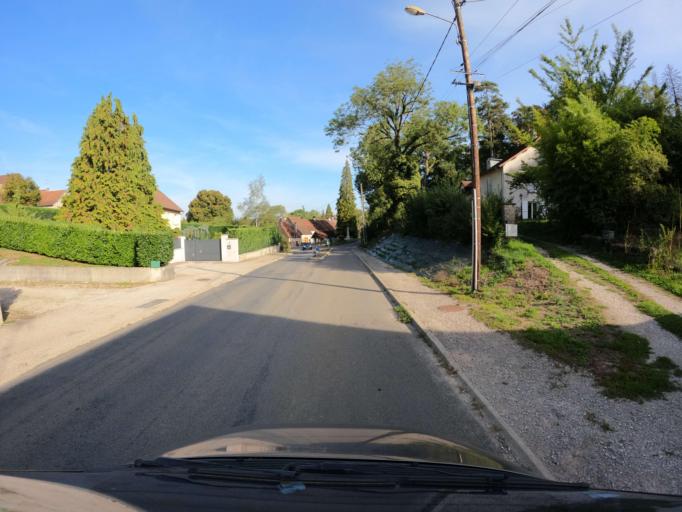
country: FR
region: Franche-Comte
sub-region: Departement du Jura
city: Montmorot
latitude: 46.7136
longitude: 5.5368
